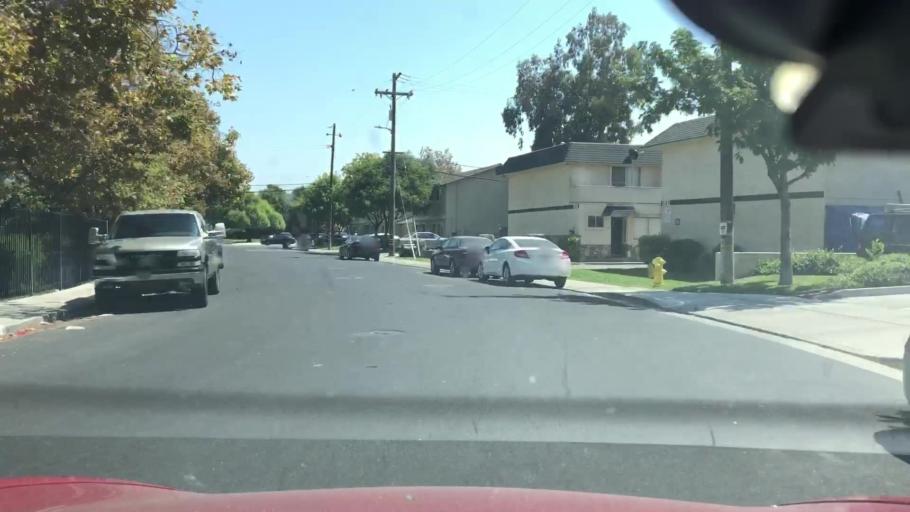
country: US
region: California
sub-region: San Joaquin County
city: Tracy
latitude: 37.7559
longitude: -121.4336
